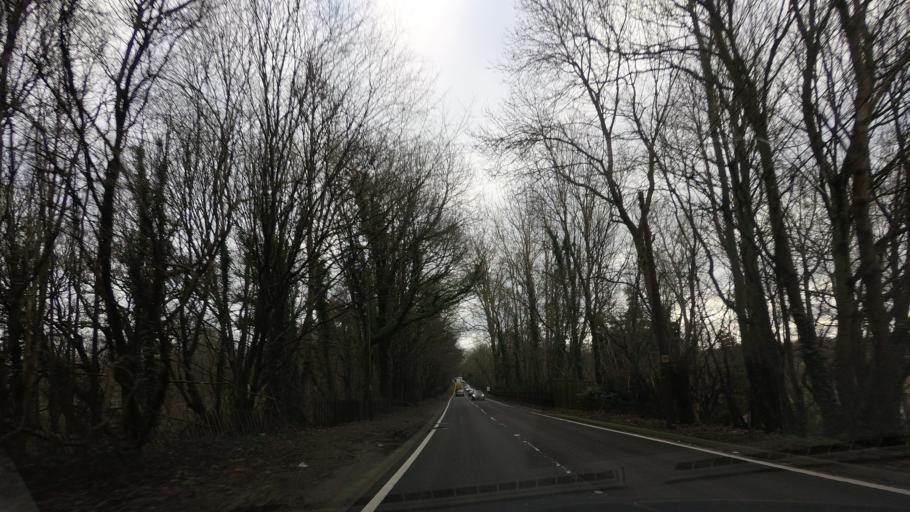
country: GB
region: England
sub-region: East Sussex
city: Wadhurst
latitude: 51.0865
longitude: 0.4064
